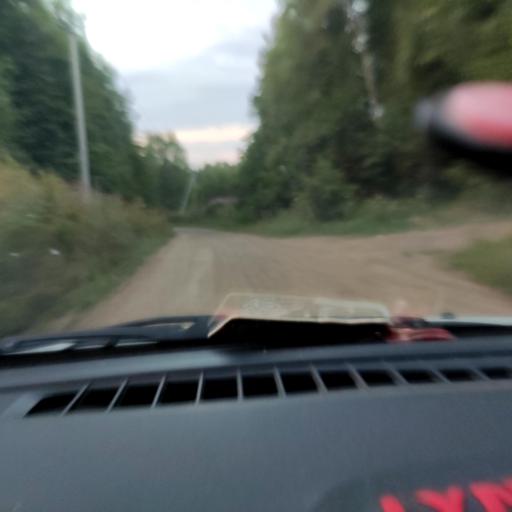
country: RU
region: Perm
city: Kukushtan
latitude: 57.6181
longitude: 56.4731
